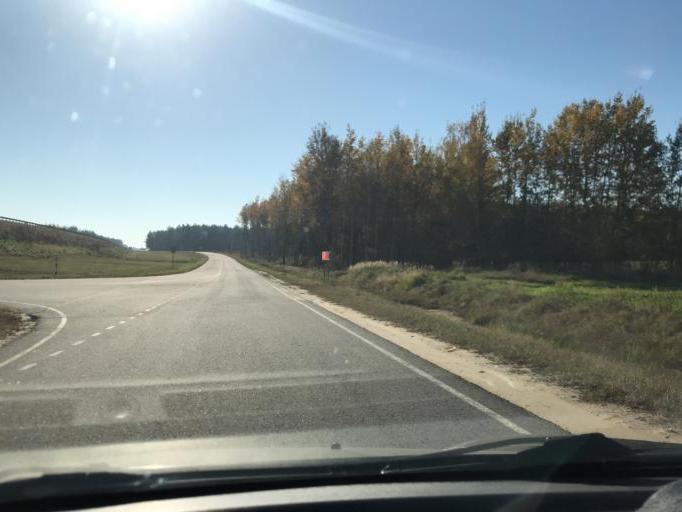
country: BY
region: Mogilev
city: Babruysk
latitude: 53.1615
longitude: 29.3590
